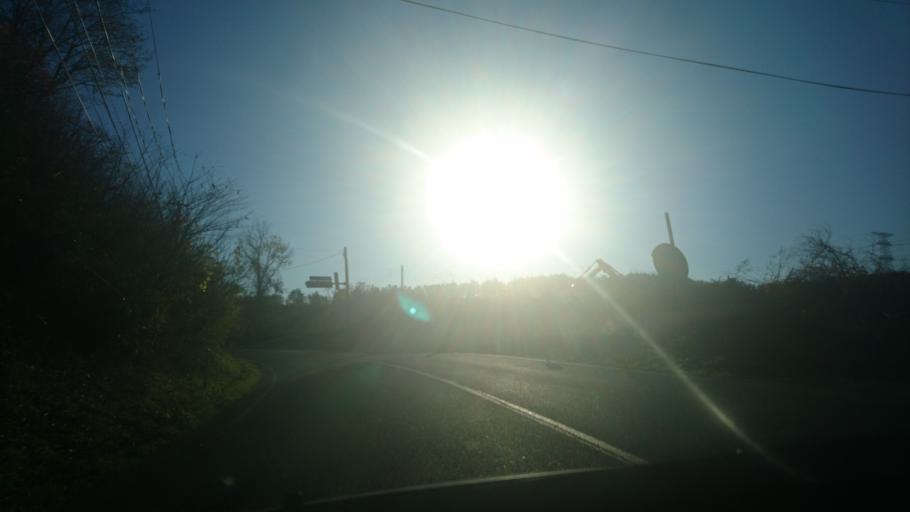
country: JP
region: Iwate
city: Ichinoseki
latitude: 38.9048
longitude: 141.2181
